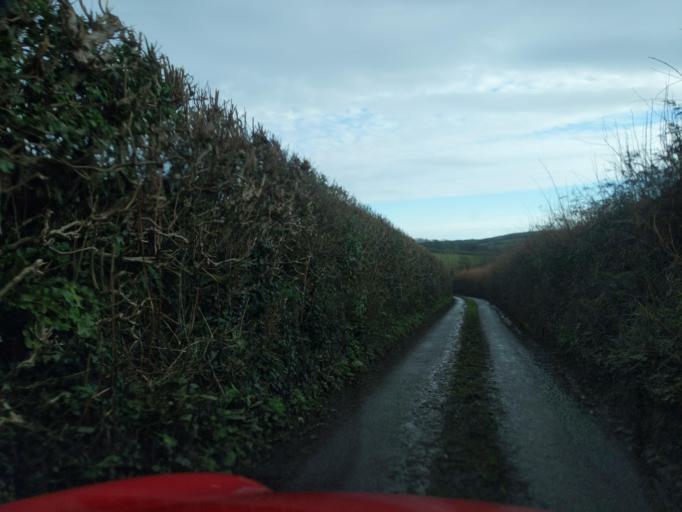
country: GB
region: England
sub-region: Devon
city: Salcombe
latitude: 50.2645
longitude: -3.6891
